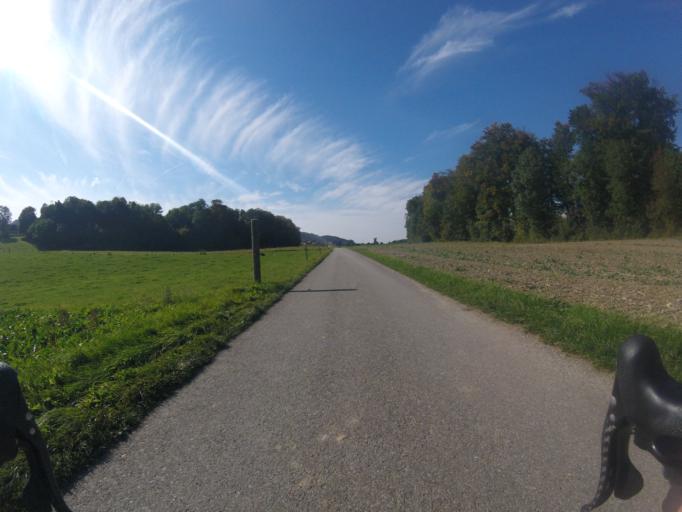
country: CH
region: Bern
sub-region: Bern-Mittelland District
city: Kehrsatz
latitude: 46.9206
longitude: 7.4765
